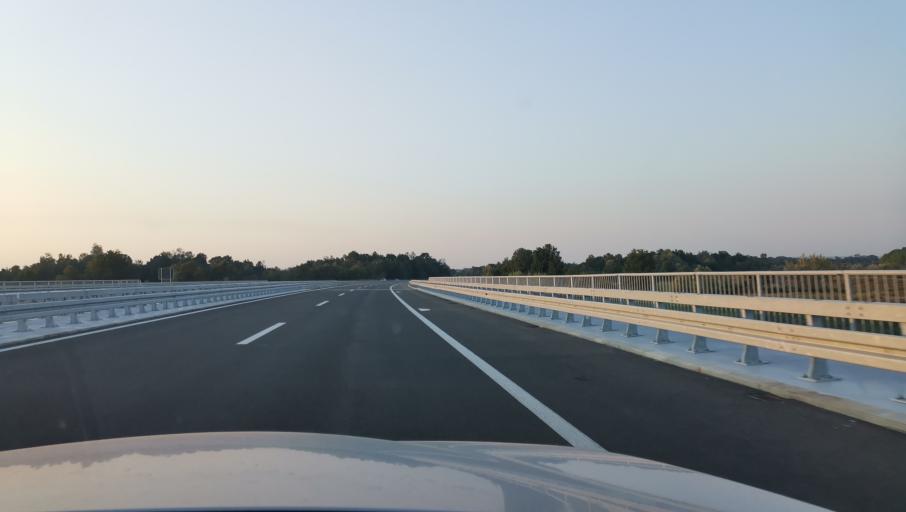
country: RS
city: Stubline
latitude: 44.5240
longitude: 20.1643
